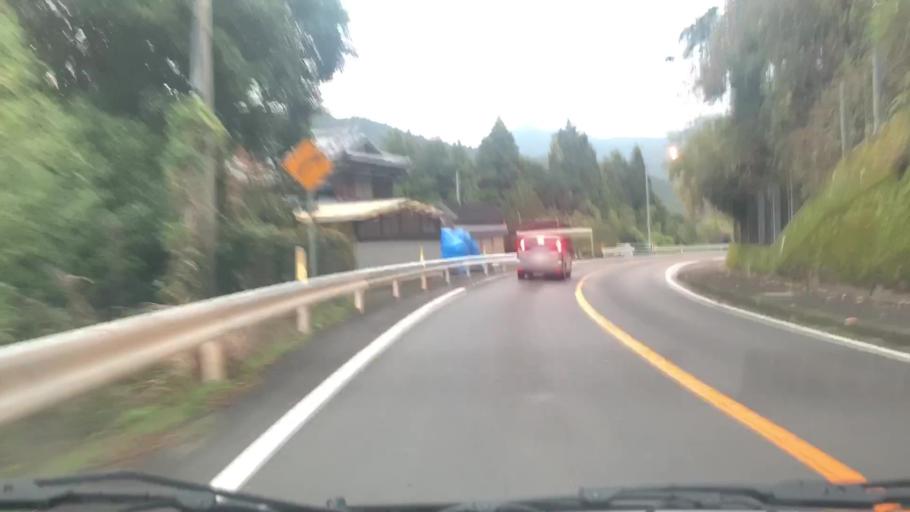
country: JP
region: Saga Prefecture
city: Ureshinomachi-shimojuku
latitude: 33.0585
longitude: 129.9490
